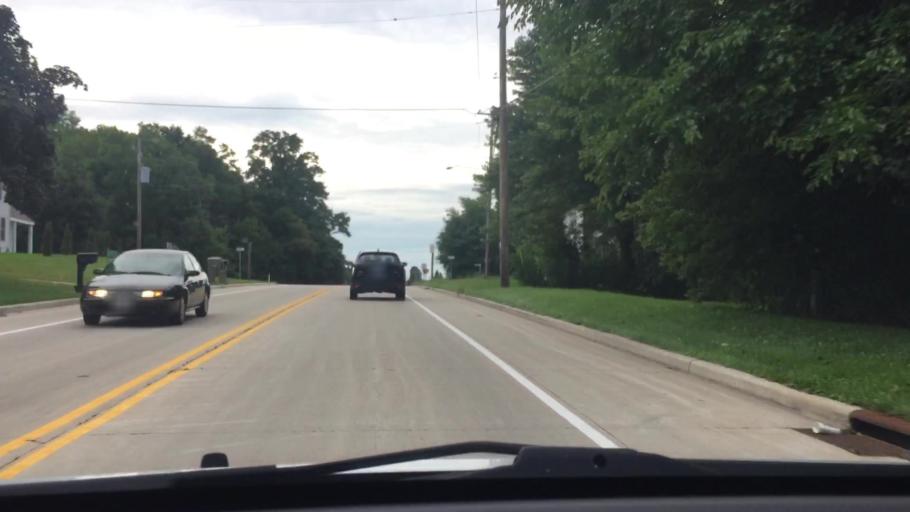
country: US
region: Wisconsin
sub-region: Waukesha County
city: North Prairie
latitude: 42.9526
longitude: -88.3566
